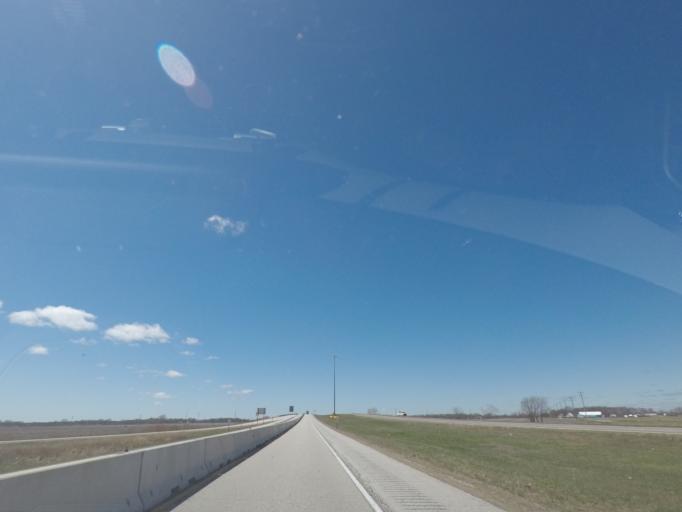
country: US
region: Illinois
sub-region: Livingston County
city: Pontiac
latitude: 40.9170
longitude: -88.6458
